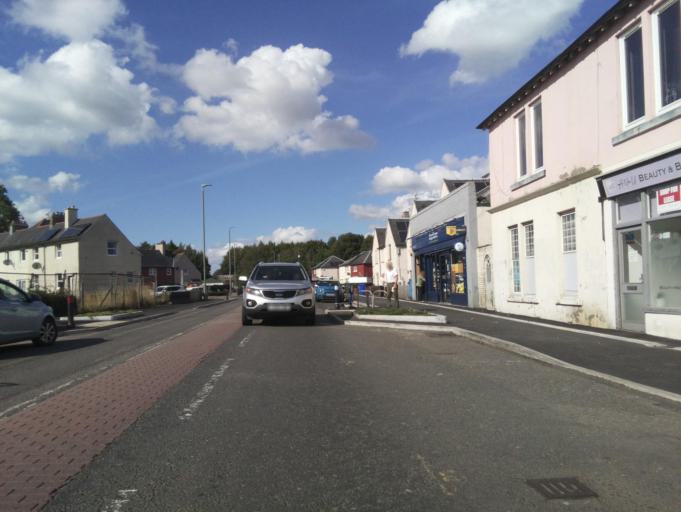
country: GB
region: Scotland
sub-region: Stirling
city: Plean
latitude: 56.0660
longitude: -3.8766
